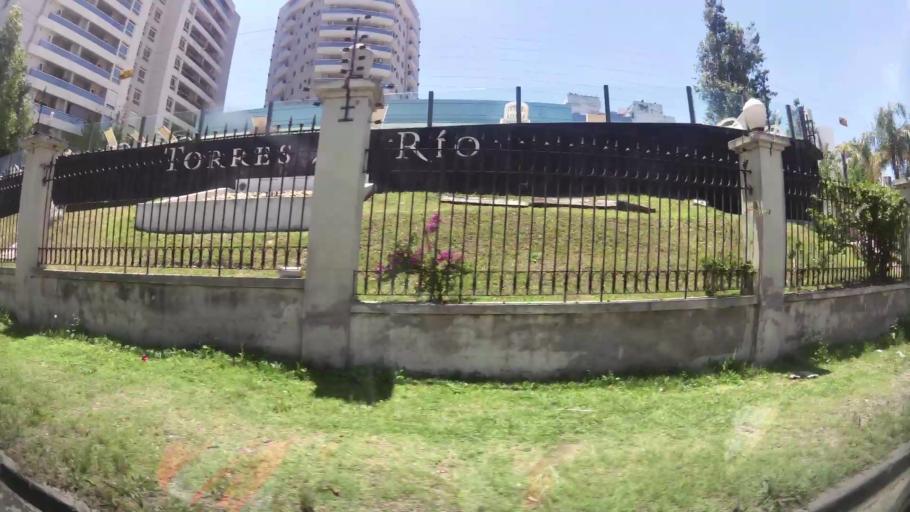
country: AR
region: Cordoba
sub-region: Departamento de Capital
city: Cordoba
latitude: -31.4044
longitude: -64.1997
